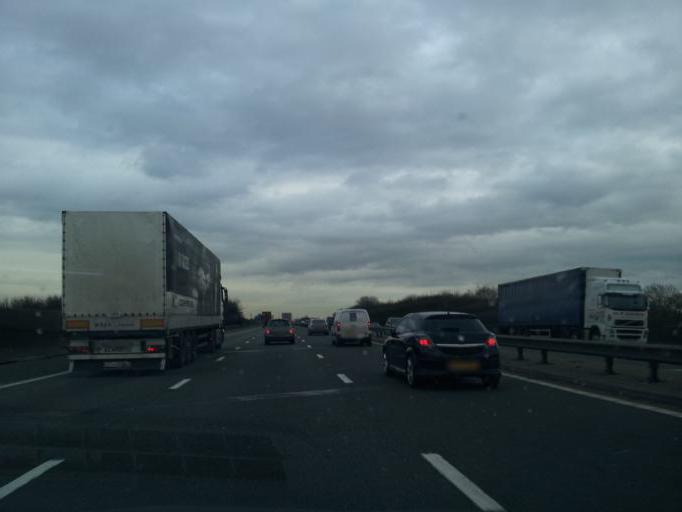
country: GB
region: England
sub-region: Warwickshire
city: Brandon
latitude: 52.4364
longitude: -1.3824
